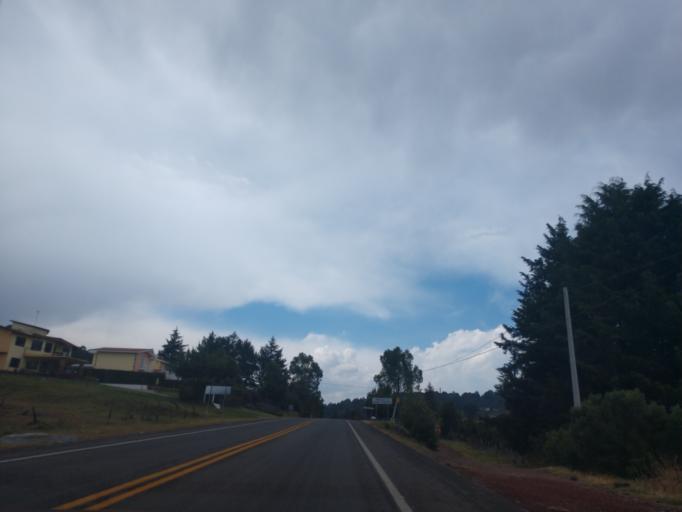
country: MX
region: Jalisco
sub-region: Mazamitla
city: Mazamitla
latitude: 19.9394
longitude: -103.0588
